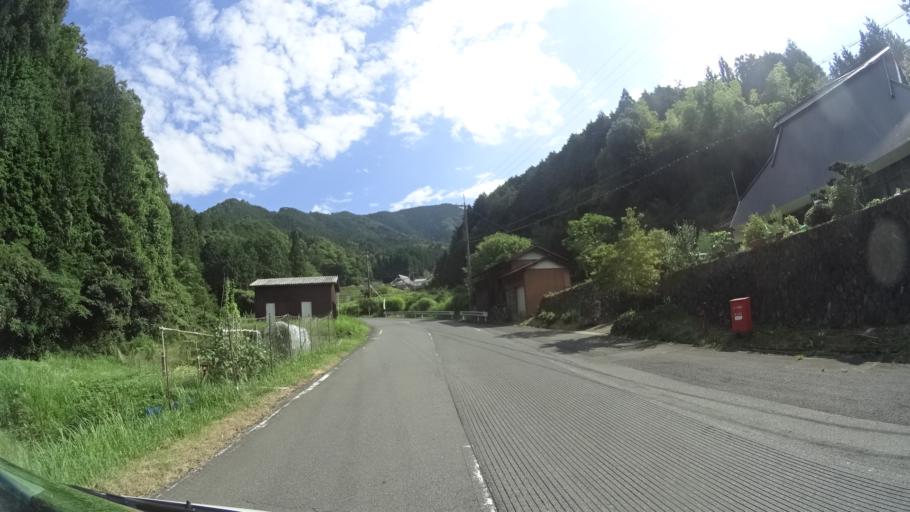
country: JP
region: Kyoto
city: Fukuchiyama
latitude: 35.3474
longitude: 135.1540
